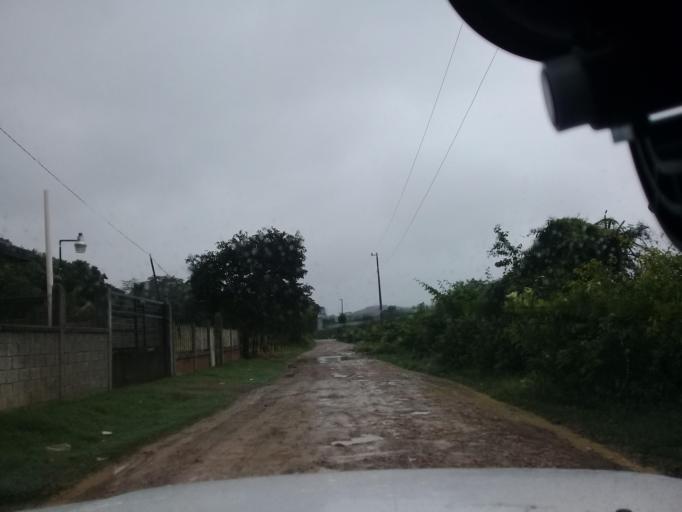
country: MX
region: Hidalgo
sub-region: Huejutla de Reyes
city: Huejutla de Reyes
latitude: 21.1779
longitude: -98.4334
